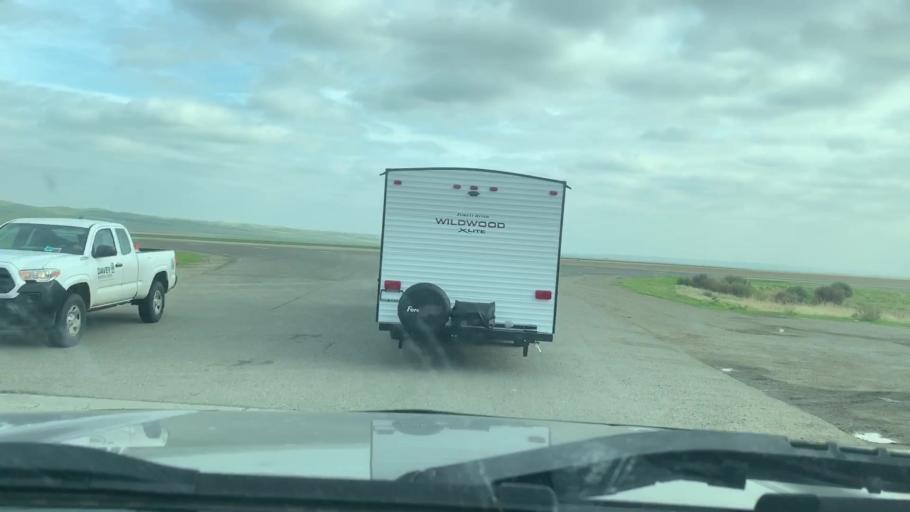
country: US
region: California
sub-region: Kings County
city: Avenal
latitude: 35.8911
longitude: -120.0457
